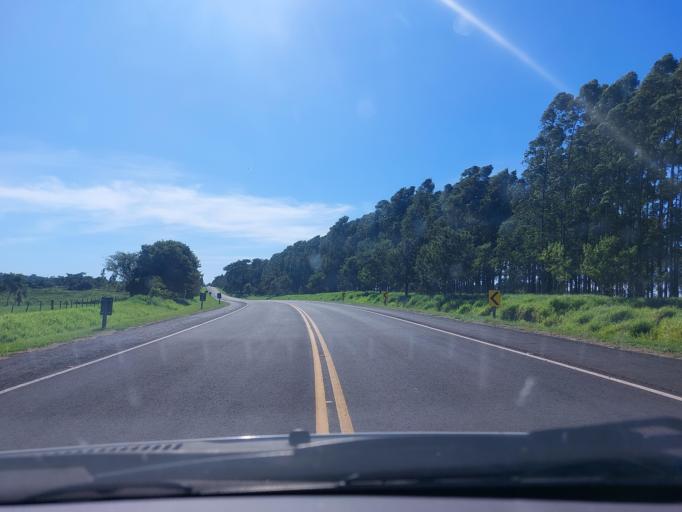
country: PY
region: San Pedro
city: Itacurubi del Rosario
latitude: -24.6032
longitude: -56.7615
